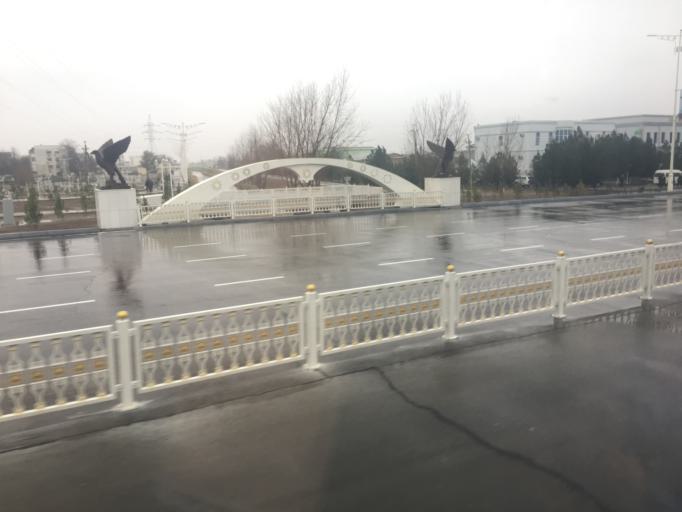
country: TM
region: Lebap
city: Turkmenabat
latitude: 39.0750
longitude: 63.5867
